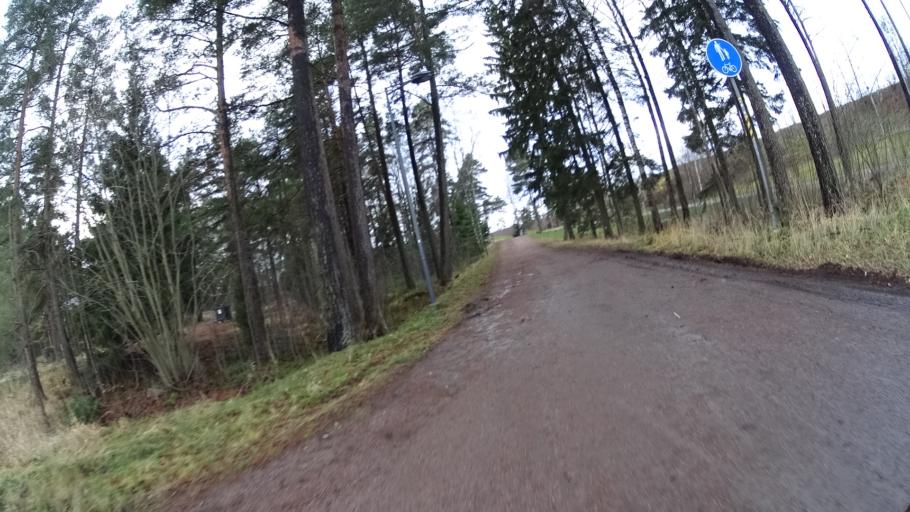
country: FI
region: Uusimaa
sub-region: Helsinki
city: Koukkuniemi
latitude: 60.1648
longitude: 24.7491
